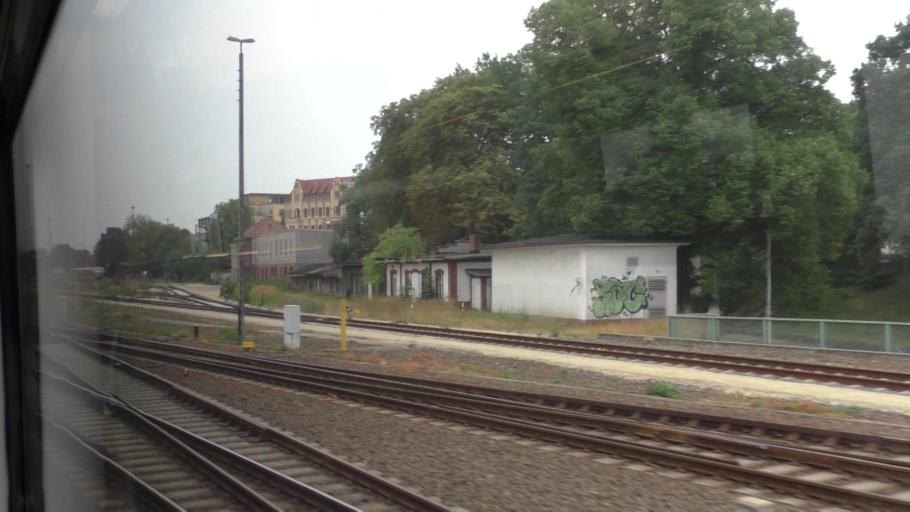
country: DE
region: Saxony
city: Goerlitz
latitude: 51.1461
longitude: 14.9813
